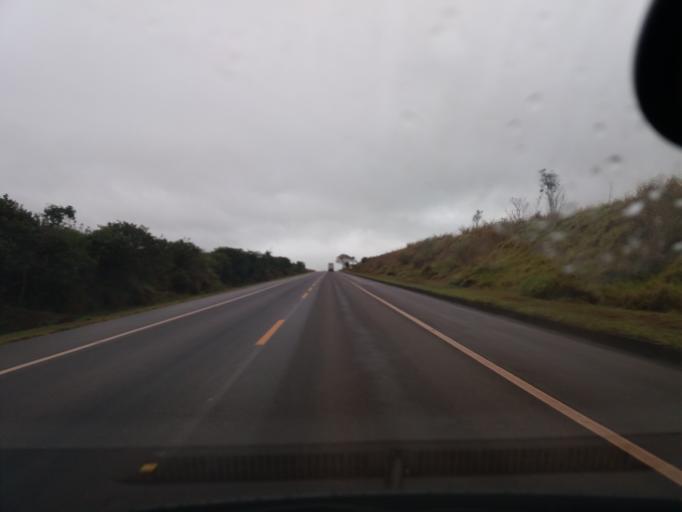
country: BR
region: Parana
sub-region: Campo Mourao
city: Campo Mourao
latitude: -24.3330
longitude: -52.6702
